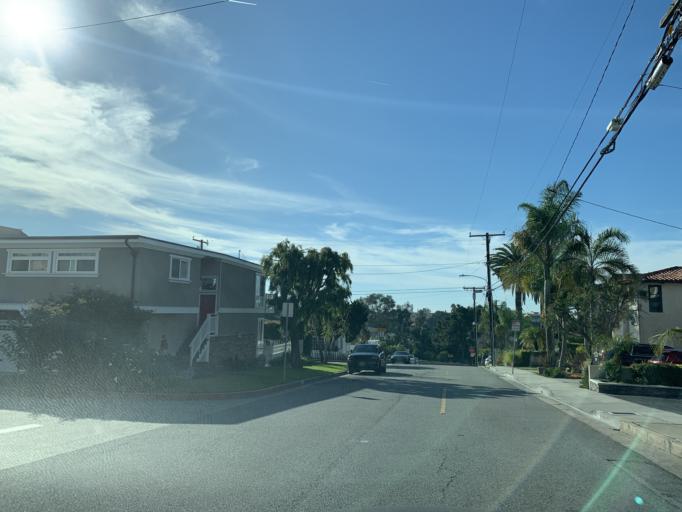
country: US
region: California
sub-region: Los Angeles County
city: Hermosa Beach
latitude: 33.8701
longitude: -118.3958
